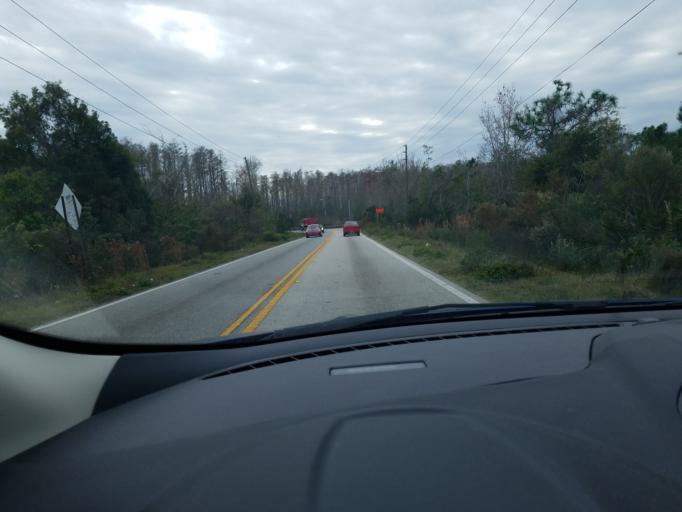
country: US
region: Florida
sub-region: Orange County
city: Hunters Creek
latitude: 28.3549
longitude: -81.3906
